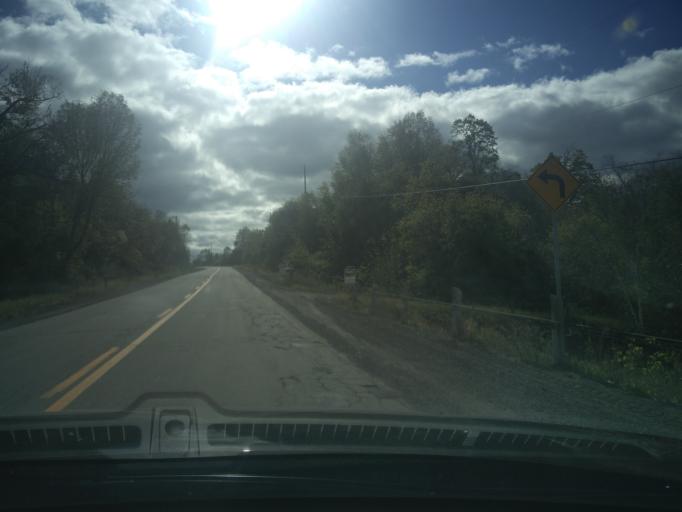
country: CA
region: Ontario
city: Perth
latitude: 44.7552
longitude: -76.3888
